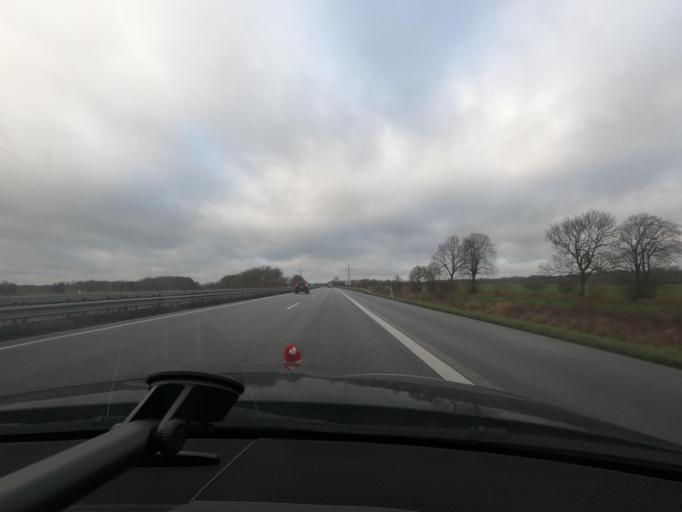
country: DE
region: Schleswig-Holstein
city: Bokel
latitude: 54.2552
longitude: 9.8045
